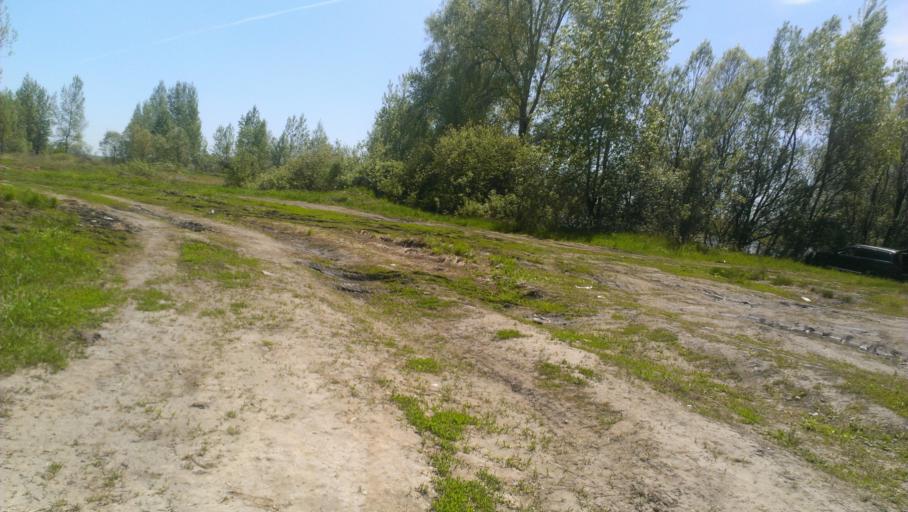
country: RU
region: Altai Krai
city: Zaton
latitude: 53.3132
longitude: 83.8524
